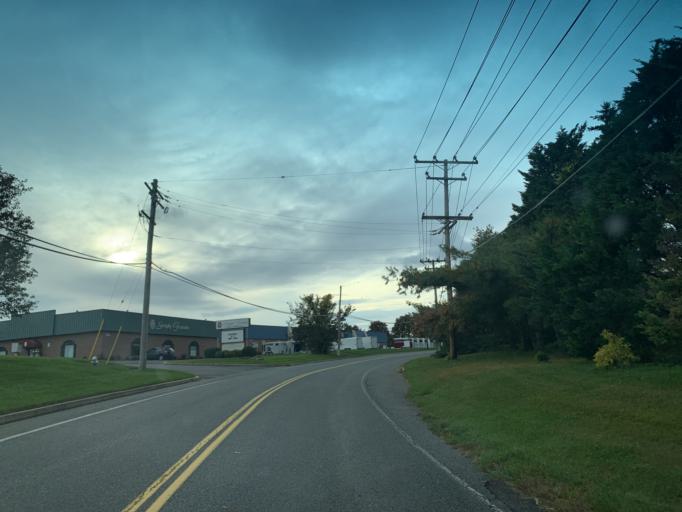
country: US
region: Maryland
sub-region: Harford County
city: Bel Air North
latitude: 39.5793
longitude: -76.3698
